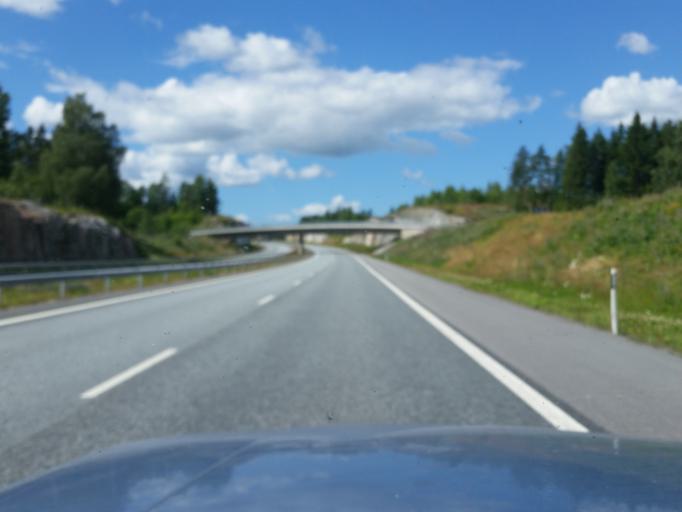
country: FI
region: Varsinais-Suomi
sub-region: Salo
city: Suomusjaervi
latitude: 60.3682
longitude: 23.6856
